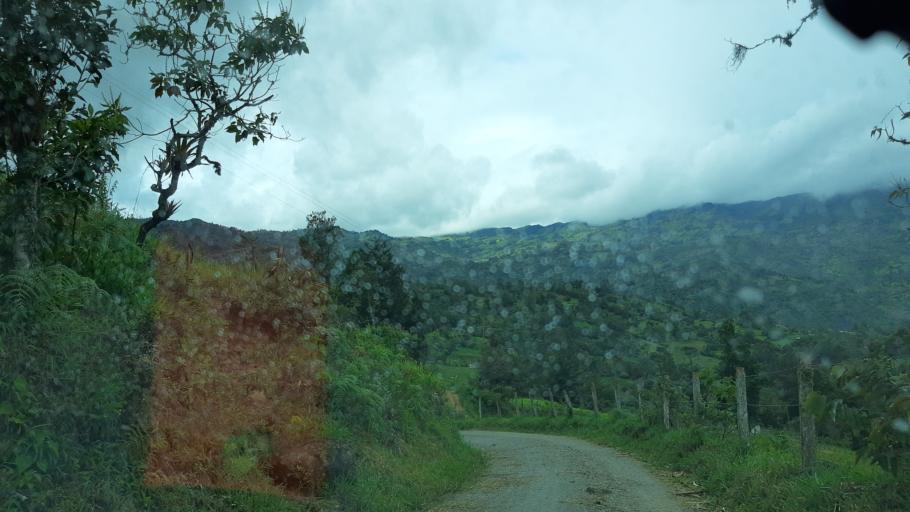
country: CO
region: Boyaca
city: Garagoa
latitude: 5.0379
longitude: -73.3590
